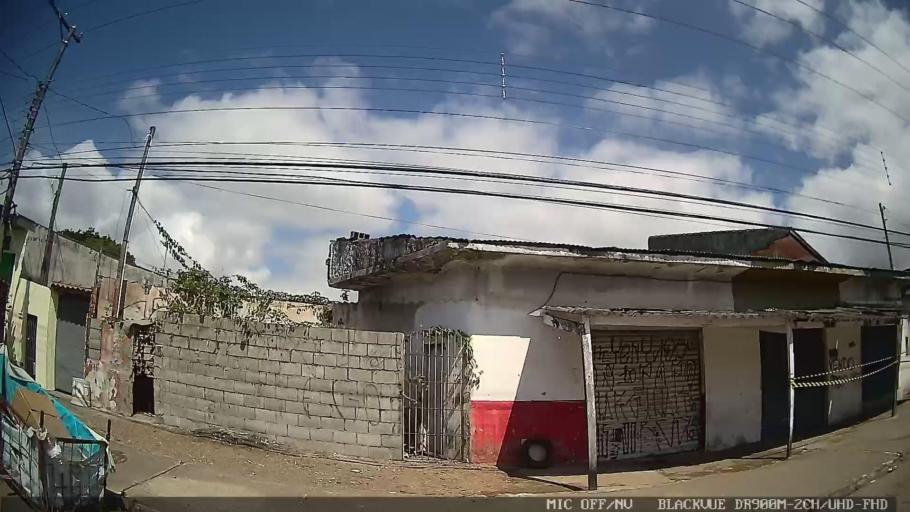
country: BR
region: Sao Paulo
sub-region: Peruibe
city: Peruibe
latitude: -24.3157
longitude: -47.0091
